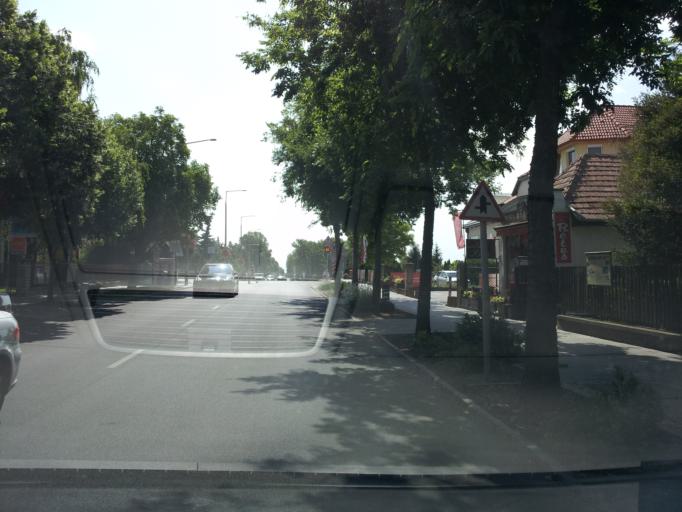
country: HU
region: Veszprem
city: Balatonfured
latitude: 46.9586
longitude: 17.8838
